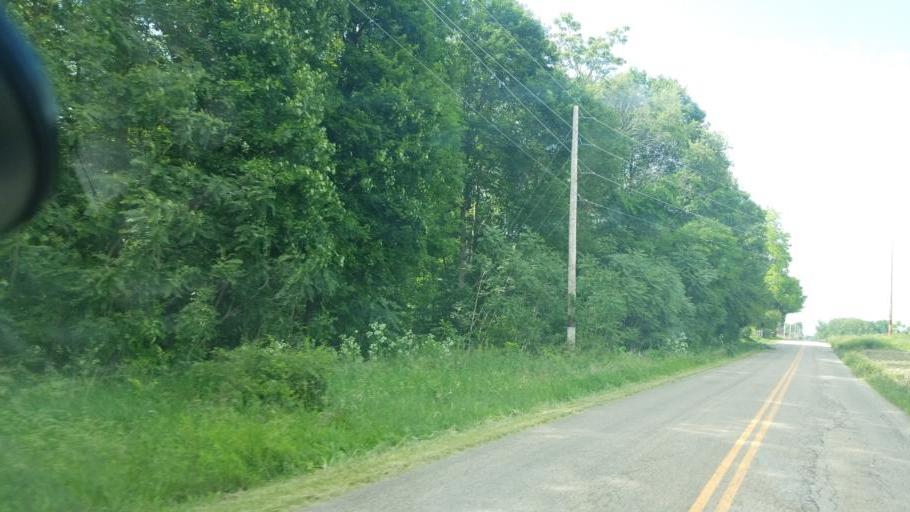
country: US
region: Ohio
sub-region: Knox County
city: Gambier
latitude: 40.3209
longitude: -82.3592
